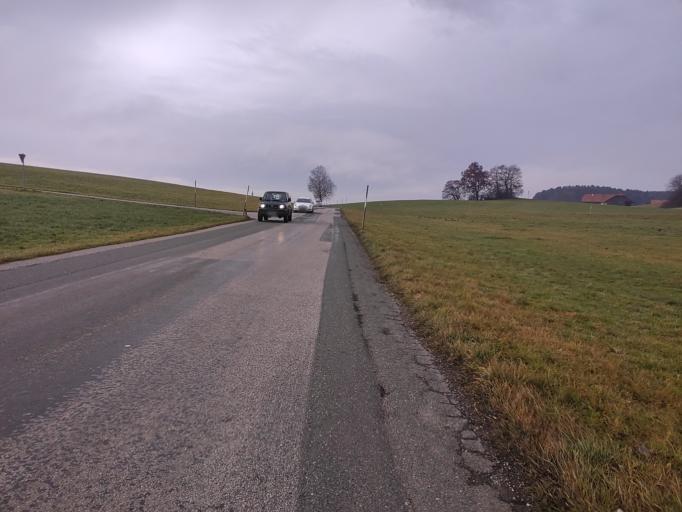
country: AT
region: Salzburg
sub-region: Politischer Bezirk Salzburg-Umgebung
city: Kostendorf
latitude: 47.9640
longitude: 13.2093
